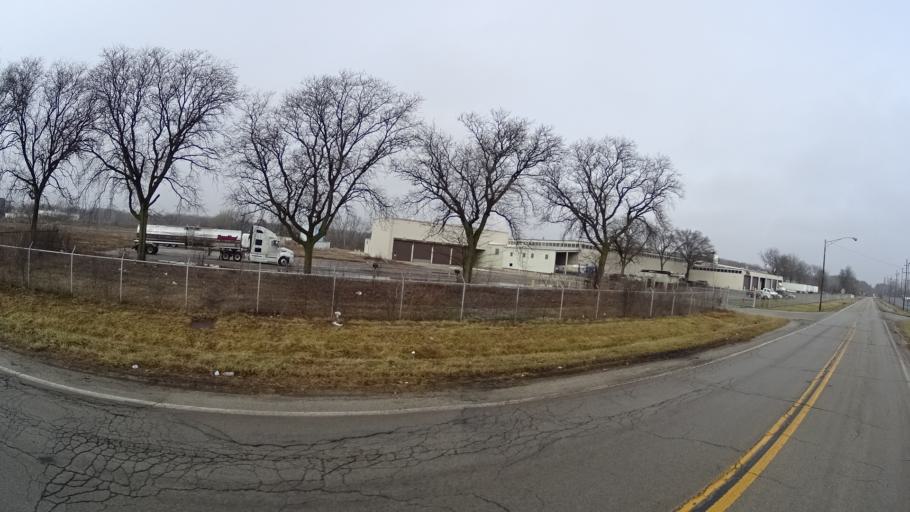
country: US
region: Illinois
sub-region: Cook County
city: Glenwood
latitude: 41.5256
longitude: -87.6165
